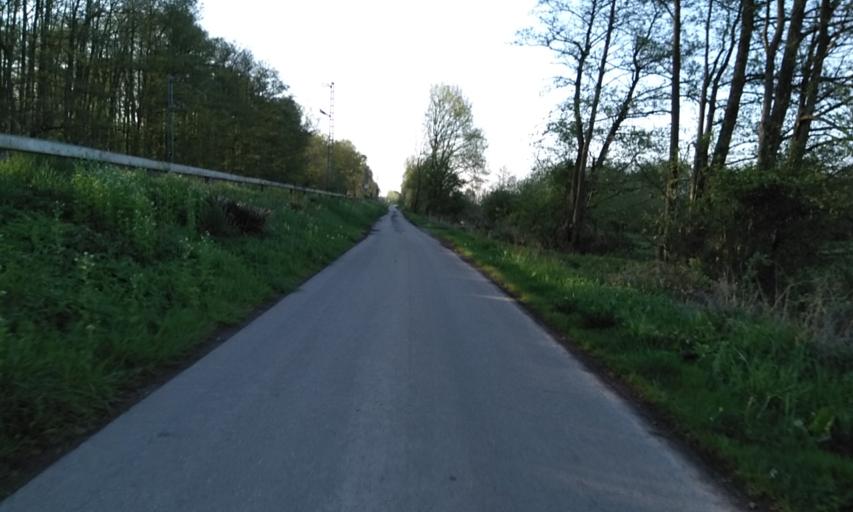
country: DE
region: Lower Saxony
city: Dollern
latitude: 53.5355
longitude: 9.5642
